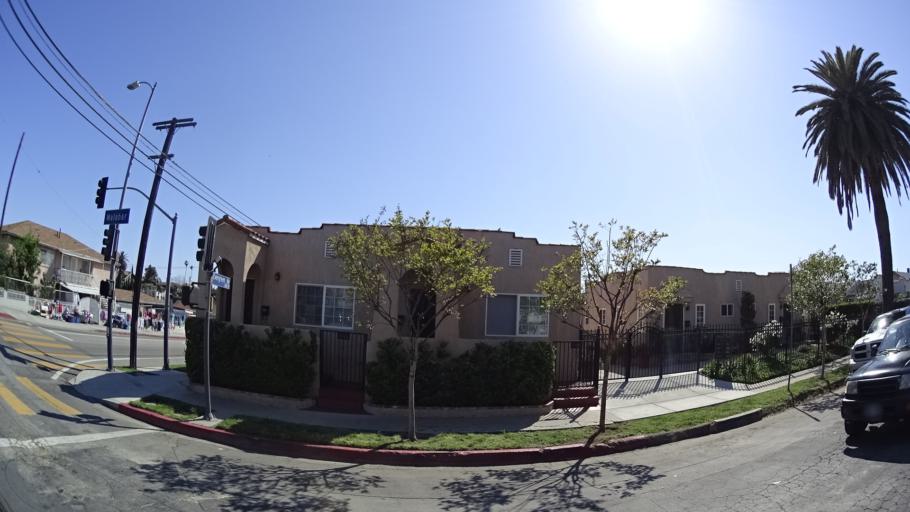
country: US
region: California
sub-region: Los Angeles County
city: Boyle Heights
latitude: 34.0467
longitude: -118.1986
